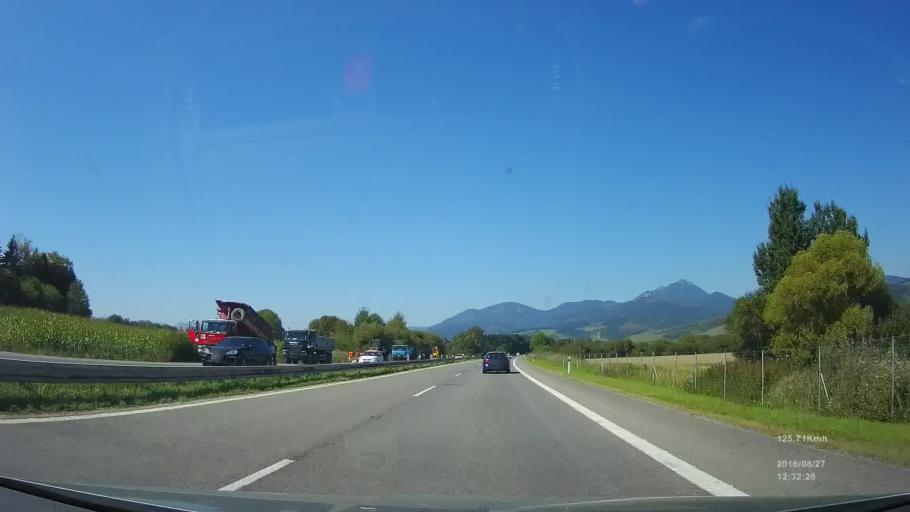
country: SK
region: Zilinsky
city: Ruzomberok
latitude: 49.0894
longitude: 19.4561
